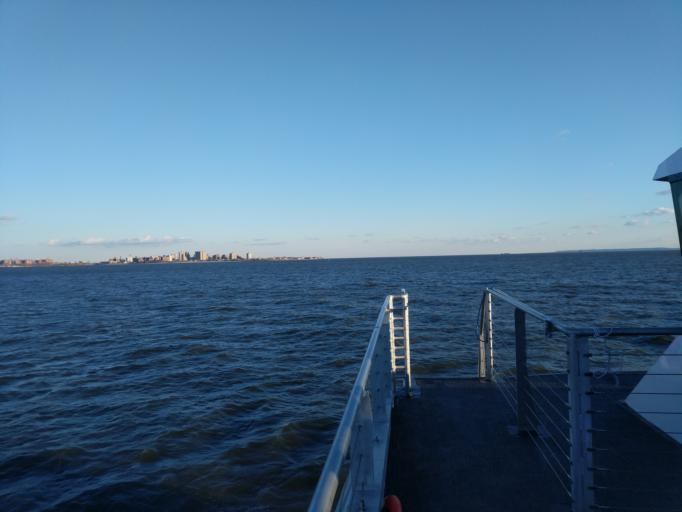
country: US
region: New York
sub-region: Kings County
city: Bensonhurst
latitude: 40.5977
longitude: -74.0325
